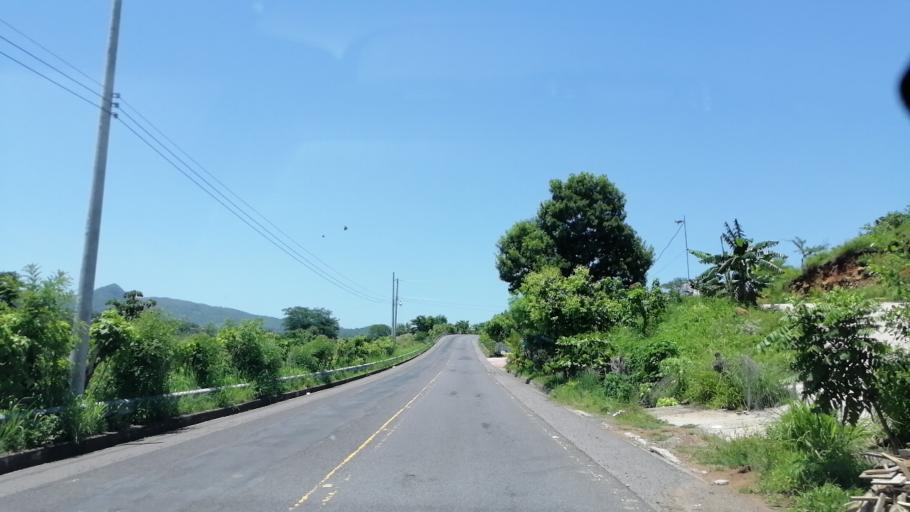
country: SV
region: Chalatenango
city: Chalatenango
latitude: 14.0302
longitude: -88.9454
